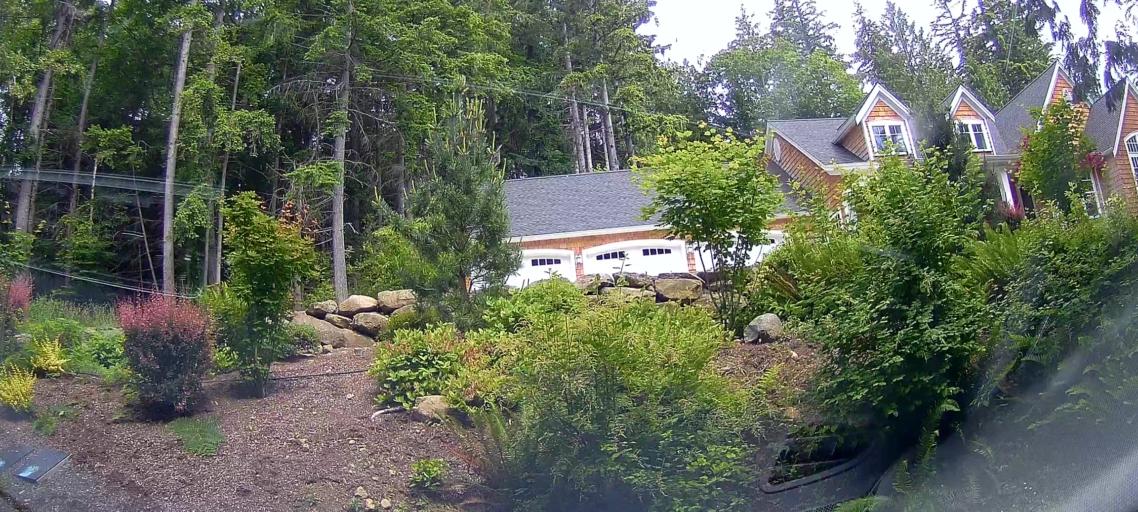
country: US
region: Washington
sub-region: Whatcom County
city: Bellingham
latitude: 48.6597
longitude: -122.4972
